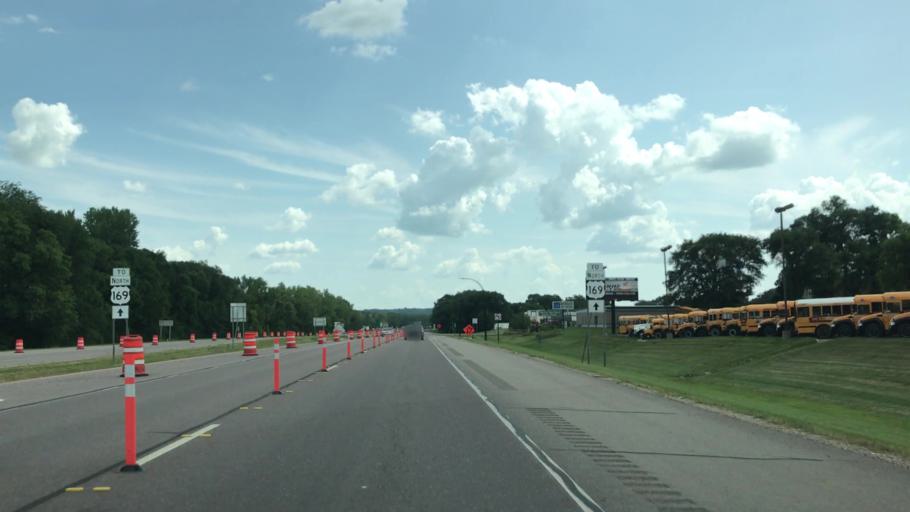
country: US
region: Minnesota
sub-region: Nicollet County
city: Saint Peter
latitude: 44.3482
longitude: -93.9515
